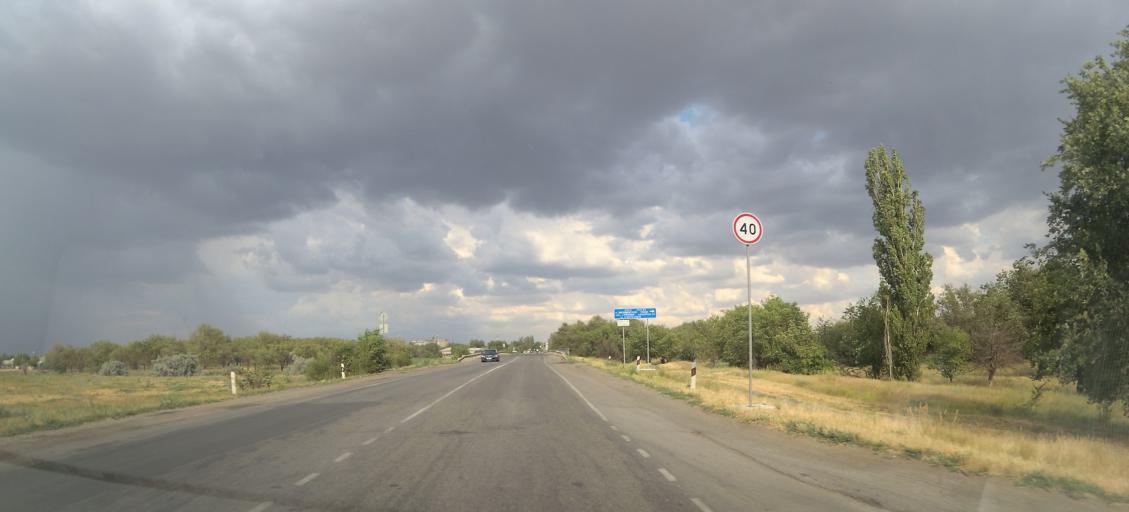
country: RU
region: Rostov
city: Zimovniki
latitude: 47.1457
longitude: 42.4474
